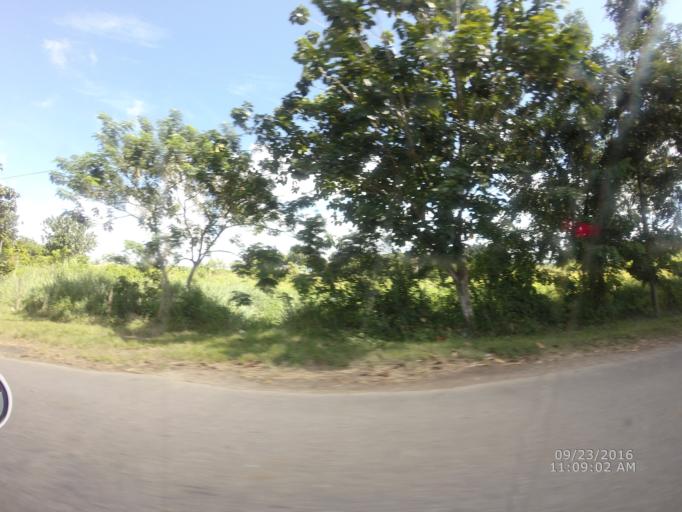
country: CU
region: La Habana
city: Arroyo Naranjo
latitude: 23.0163
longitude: -82.2389
